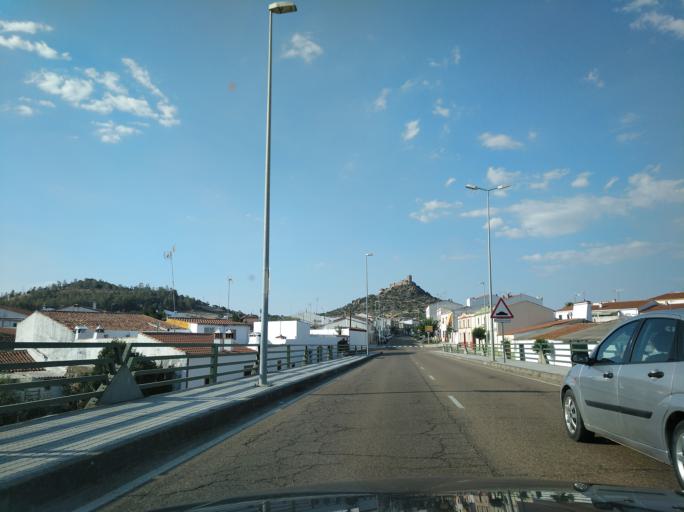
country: ES
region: Extremadura
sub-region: Provincia de Badajoz
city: Alconchel
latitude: 38.5123
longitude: -7.0698
